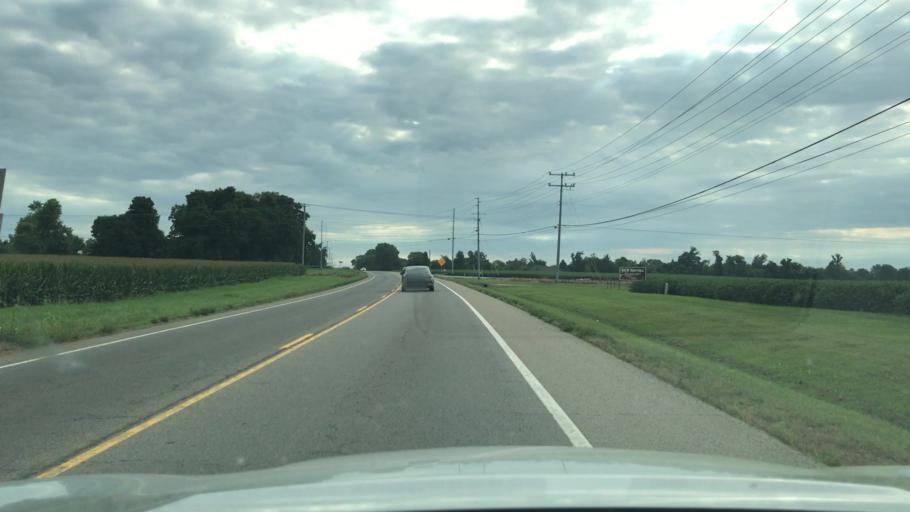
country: US
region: Kentucky
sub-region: Todd County
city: Guthrie
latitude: 36.6120
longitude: -87.2478
